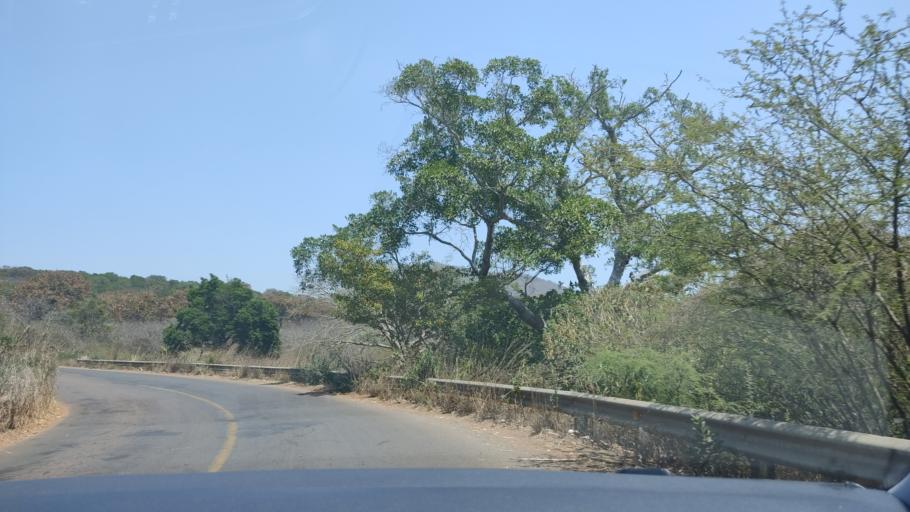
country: MX
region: Nayarit
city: Puga
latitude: 21.5785
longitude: -104.7781
